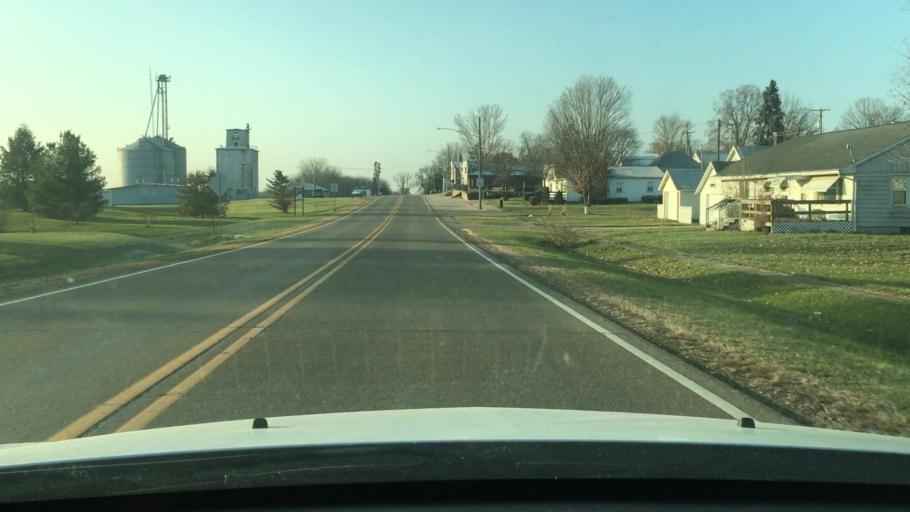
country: US
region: Illinois
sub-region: Woodford County
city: Washburn
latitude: 40.9837
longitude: -89.2345
